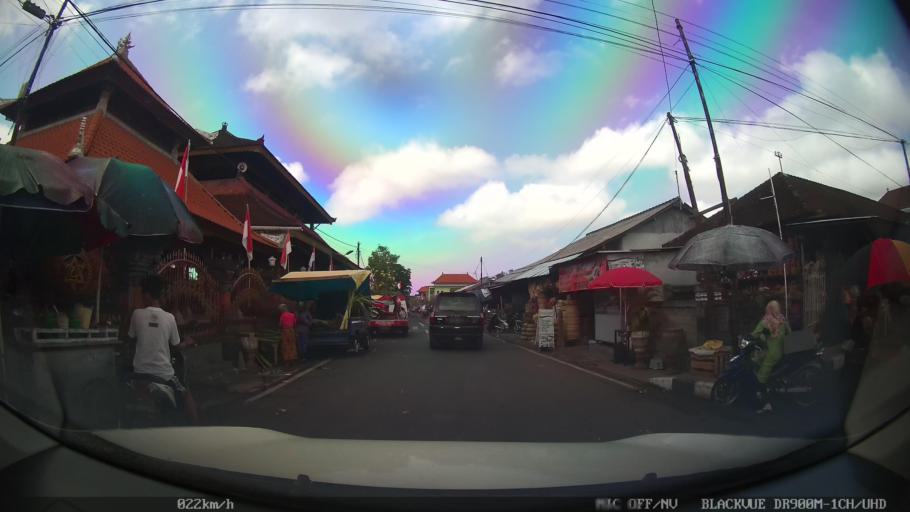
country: ID
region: Bali
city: Banjar Pasekan
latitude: -8.5959
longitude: 115.2845
